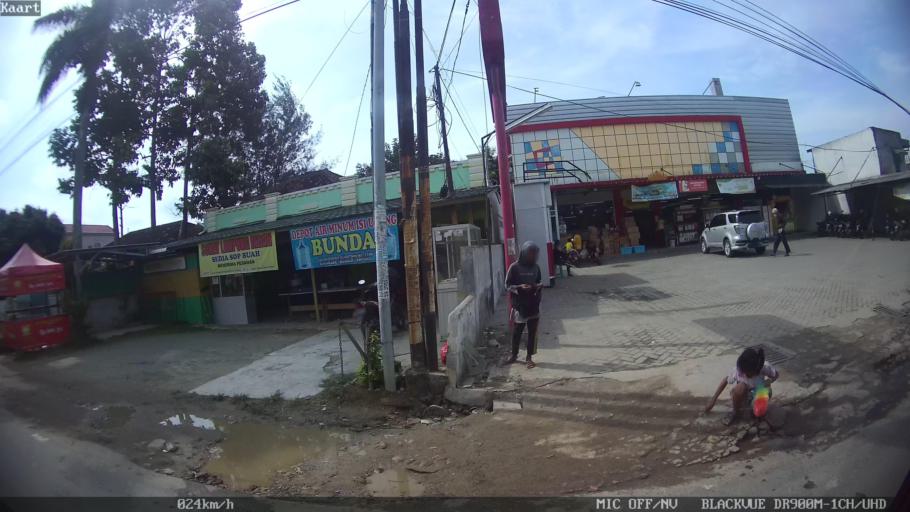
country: ID
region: Lampung
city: Kedaton
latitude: -5.3868
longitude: 105.2921
